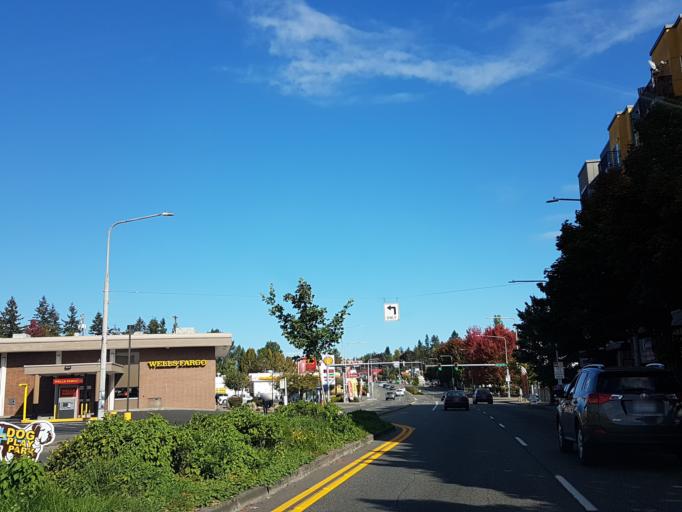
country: US
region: Washington
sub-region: King County
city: Lake Forest Park
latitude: 47.7218
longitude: -122.2937
